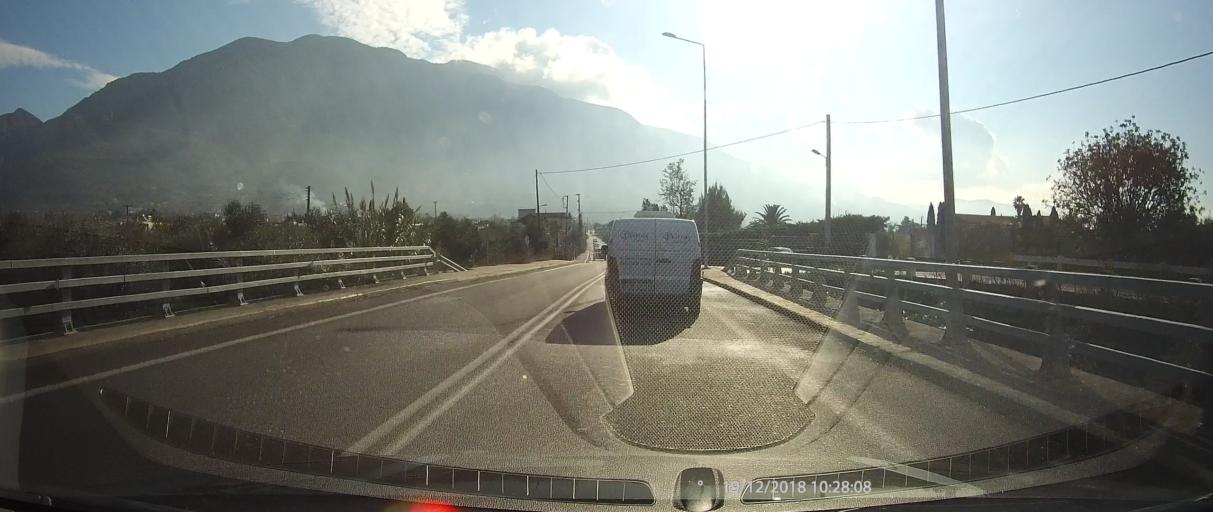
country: GR
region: Peloponnese
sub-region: Nomos Messinias
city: Kalamata
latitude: 37.0297
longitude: 22.1391
